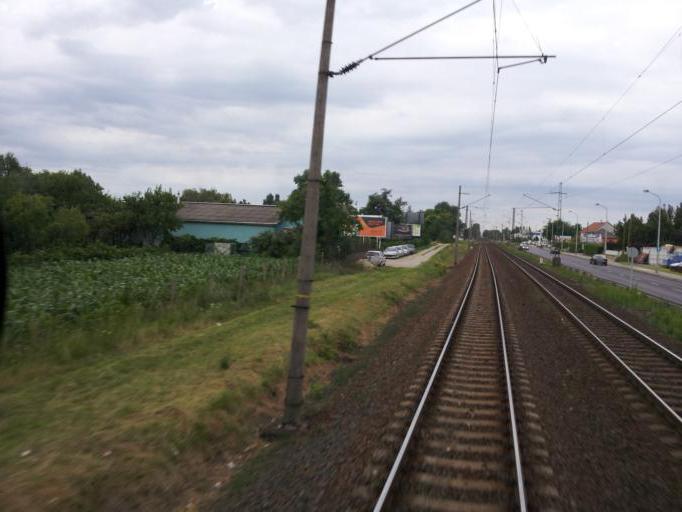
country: HU
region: Fejer
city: Szekesfehervar
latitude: 47.1707
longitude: 18.4056
